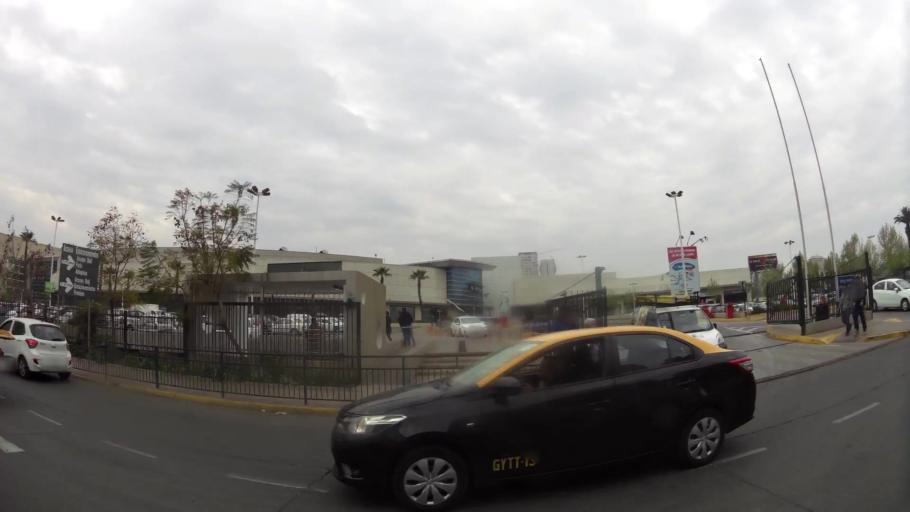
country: CL
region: Santiago Metropolitan
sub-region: Provincia de Santiago
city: Villa Presidente Frei, Nunoa, Santiago, Chile
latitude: -33.5170
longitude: -70.6005
